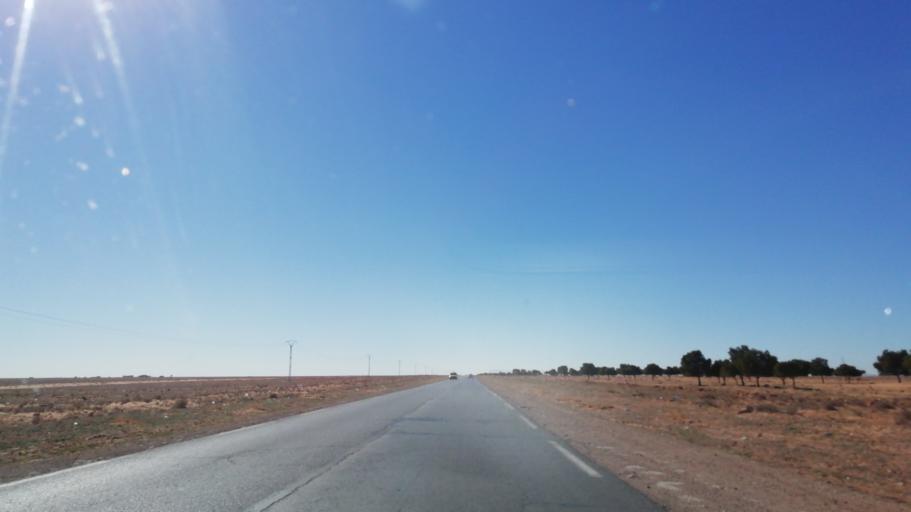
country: DZ
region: Saida
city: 'Ain el Hadjar
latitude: 33.9950
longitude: 0.0390
